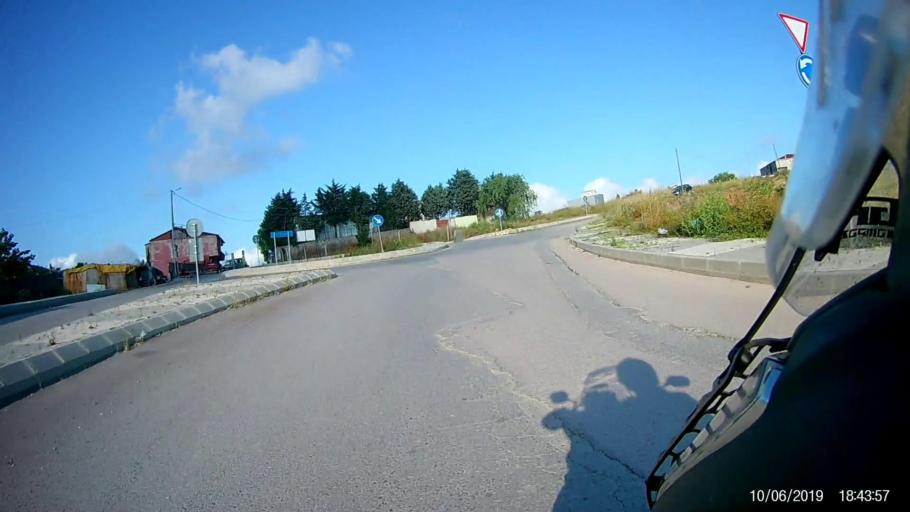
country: TR
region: Istanbul
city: Sancaktepe
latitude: 41.0376
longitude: 29.2687
